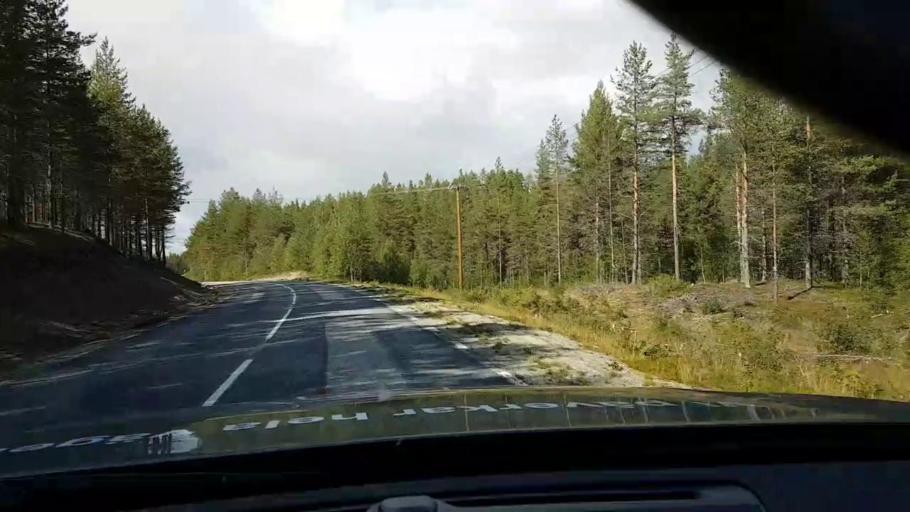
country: SE
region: Vaesterbotten
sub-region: Asele Kommun
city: Asele
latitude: 63.8532
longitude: 17.3923
